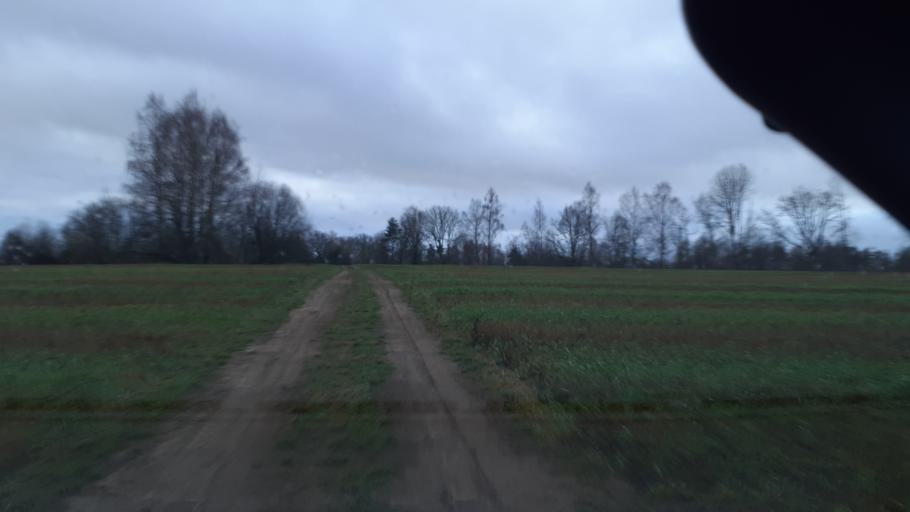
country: LV
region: Kuldigas Rajons
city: Kuldiga
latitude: 56.8821
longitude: 21.7705
